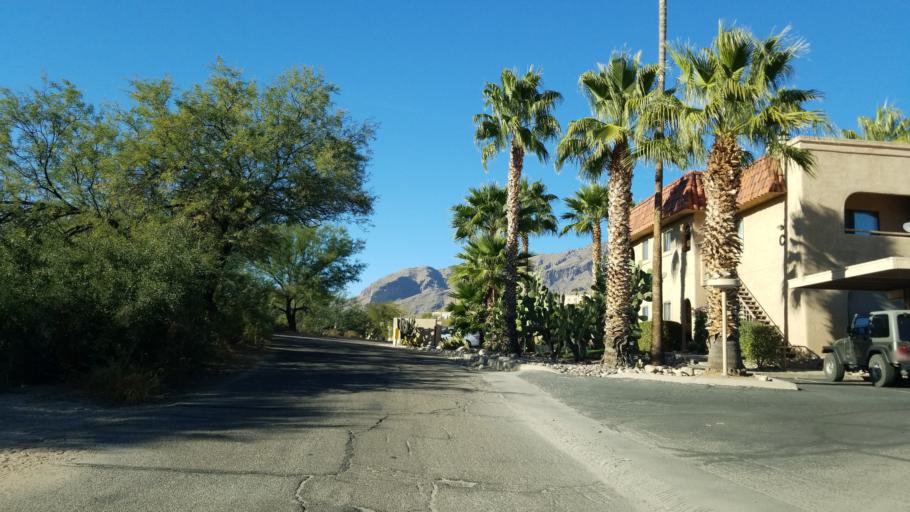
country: US
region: Arizona
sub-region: Pima County
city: Catalina Foothills
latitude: 32.3104
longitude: -110.8897
